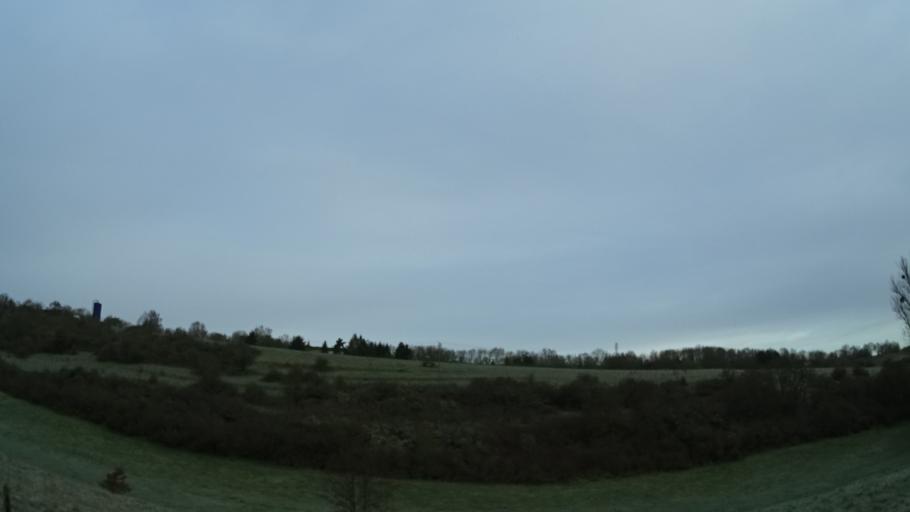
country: DE
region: Rheinland-Pfalz
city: Daubach
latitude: 49.8469
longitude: 7.6441
